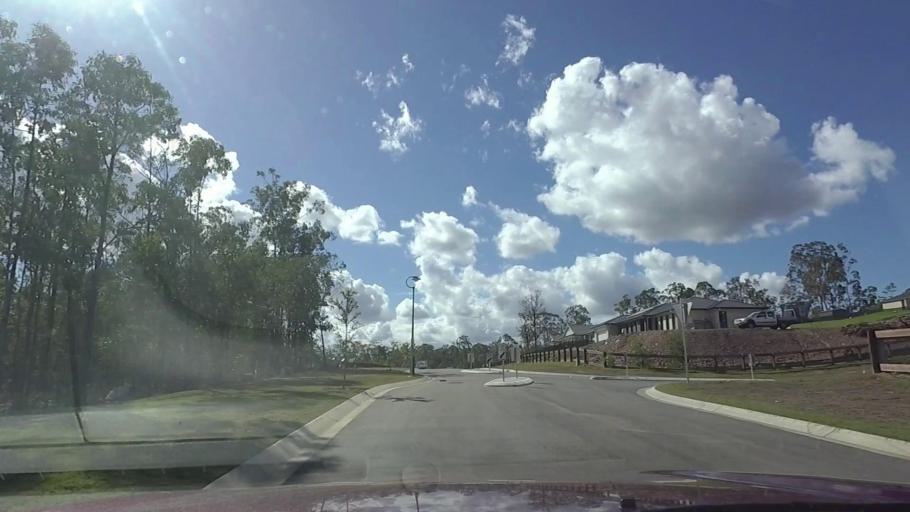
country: AU
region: Queensland
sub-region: Ipswich
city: Springfield Lakes
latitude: -27.7535
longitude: 152.9193
